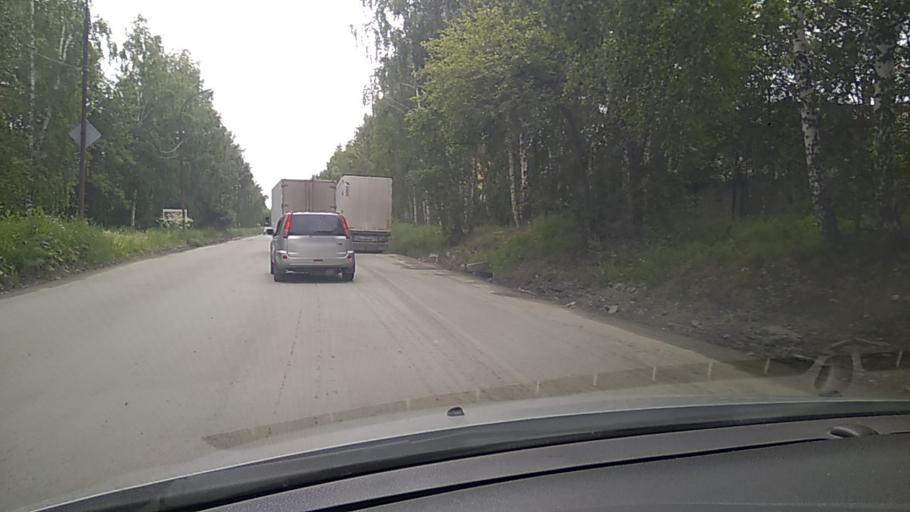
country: RU
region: Sverdlovsk
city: Shuvakish
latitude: 56.8924
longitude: 60.5159
